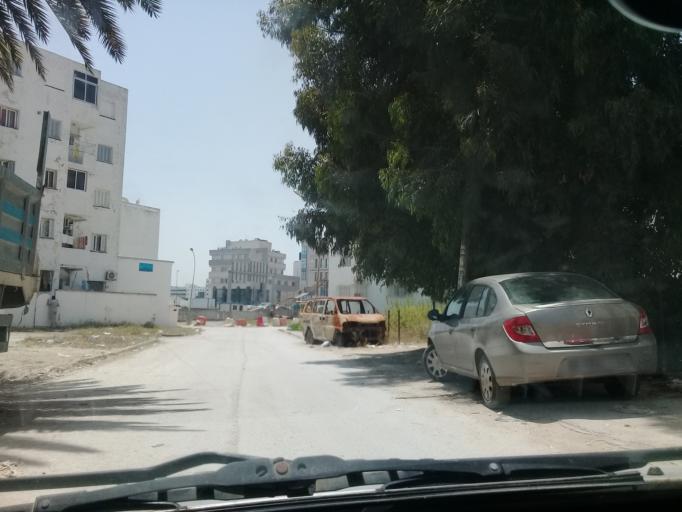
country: TN
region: Tunis
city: Tunis
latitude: 36.8274
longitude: 10.1948
